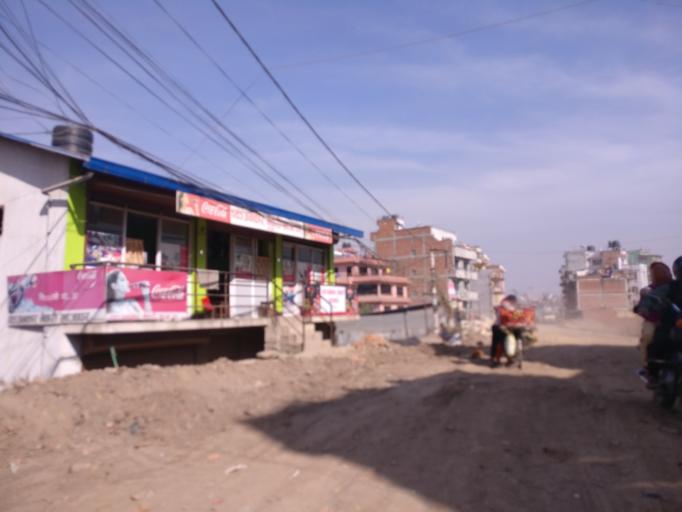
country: NP
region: Central Region
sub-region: Bagmati Zone
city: Patan
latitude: 27.6751
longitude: 85.3308
